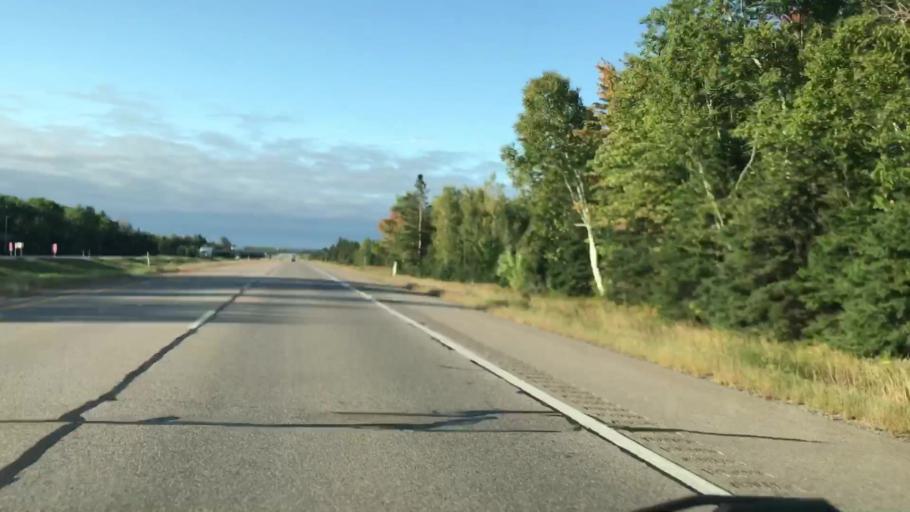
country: US
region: Michigan
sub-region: Chippewa County
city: Sault Ste. Marie
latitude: 46.4250
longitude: -84.3931
